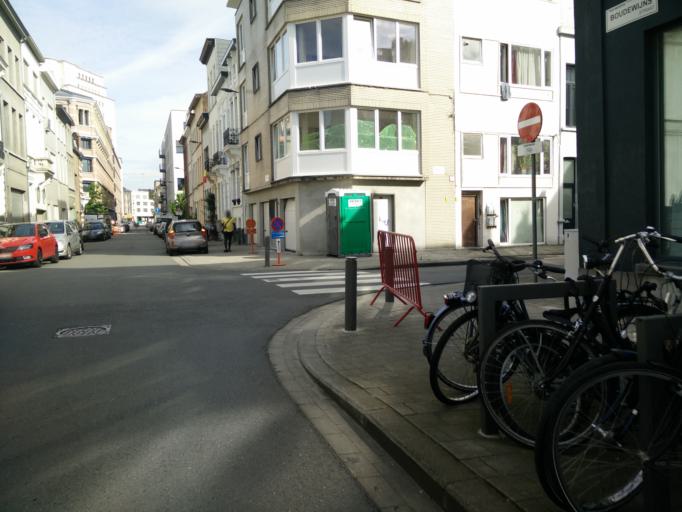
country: BE
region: Flanders
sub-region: Provincie Antwerpen
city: Antwerpen
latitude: 51.2045
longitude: 4.4011
